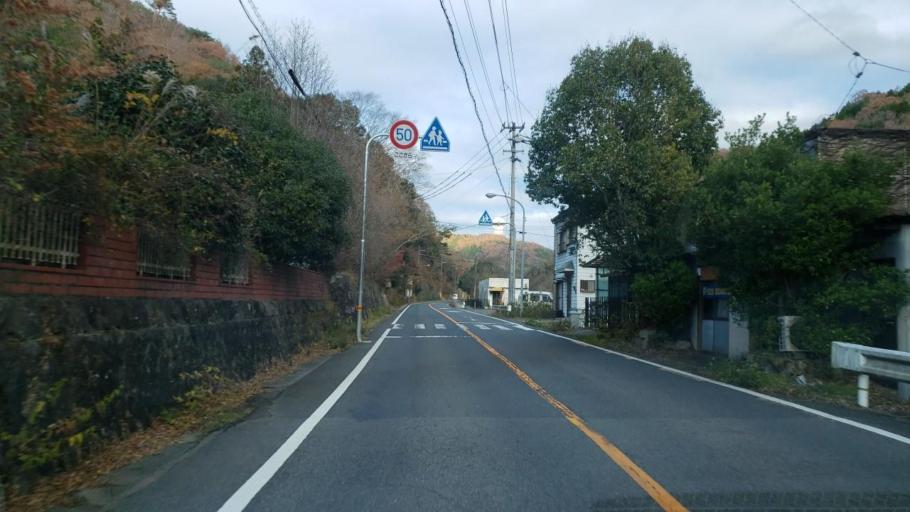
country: JP
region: Tokushima
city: Wakimachi
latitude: 34.1685
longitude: 134.0870
